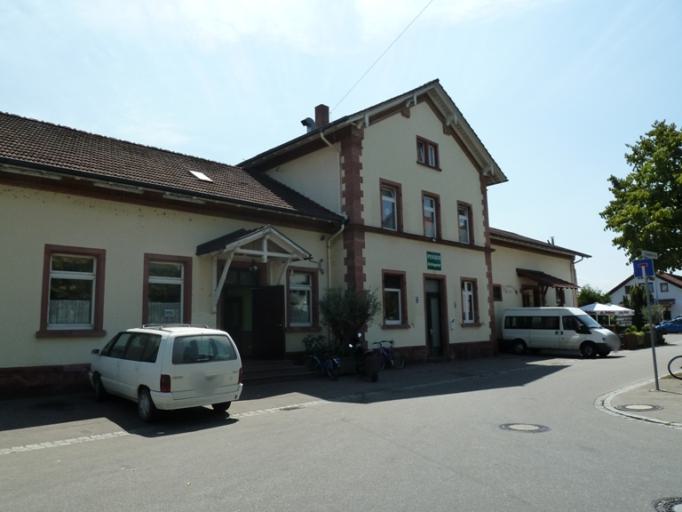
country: DE
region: Baden-Wuerttemberg
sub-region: Freiburg Region
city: Weil am Rhein
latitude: 47.5909
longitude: 7.6347
